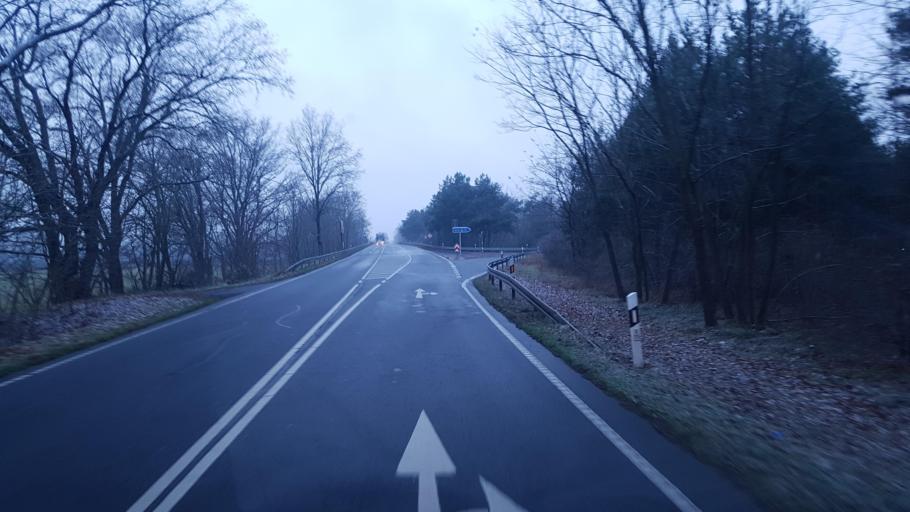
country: DE
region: Brandenburg
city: Kasel-Golzig
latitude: 51.9533
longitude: 13.7715
